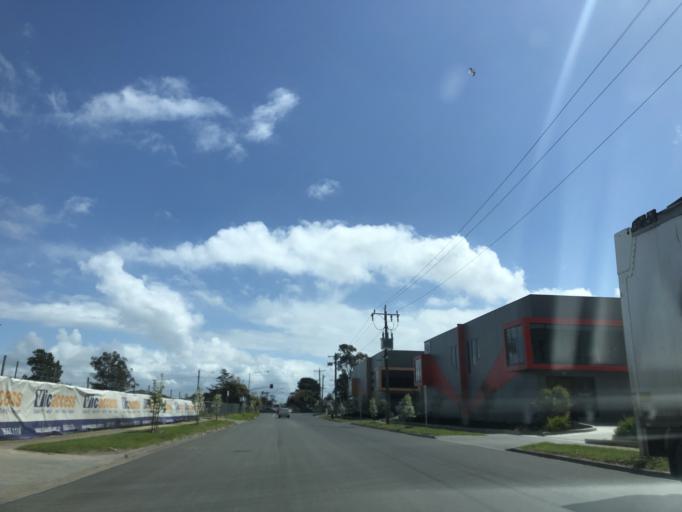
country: AU
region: Victoria
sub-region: Kingston
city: Clayton South
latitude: -37.9432
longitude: 145.1182
